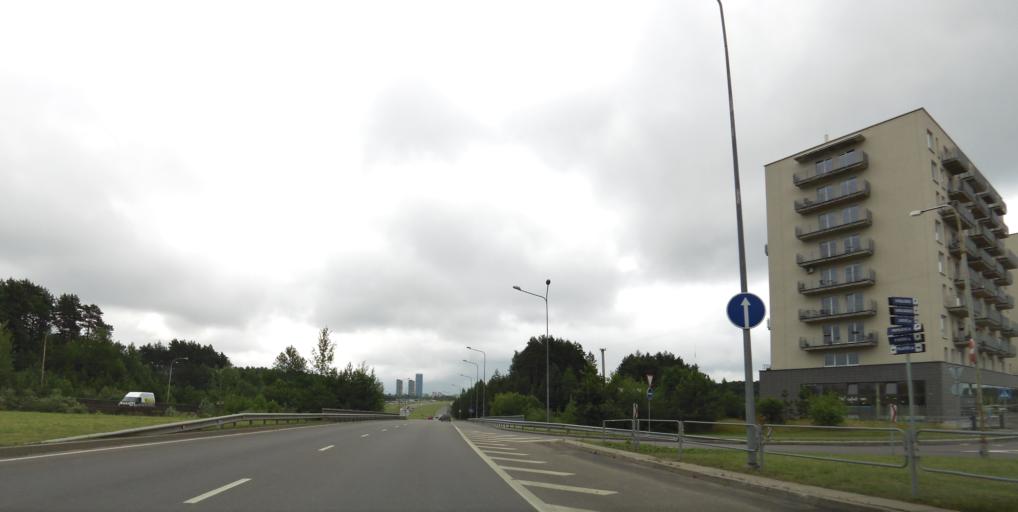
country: LT
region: Vilnius County
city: Pilaite
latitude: 54.7082
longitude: 25.1892
